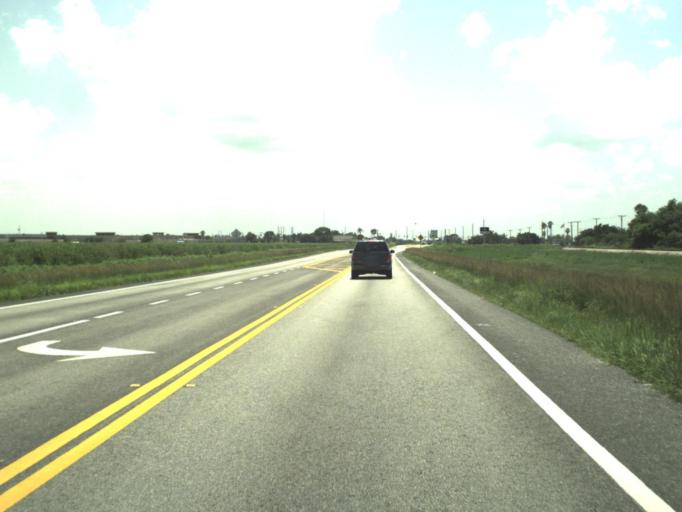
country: US
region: Florida
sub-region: Palm Beach County
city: Belle Glade
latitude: 26.7326
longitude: -80.6645
